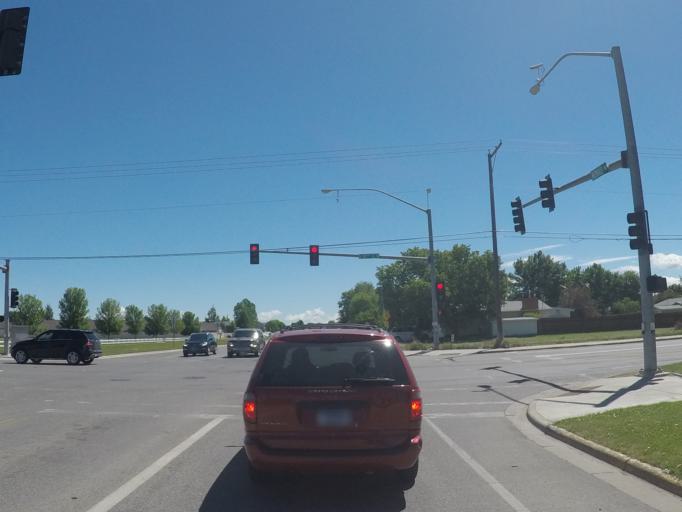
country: US
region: Montana
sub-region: Yellowstone County
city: Billings
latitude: 45.7623
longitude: -108.5973
